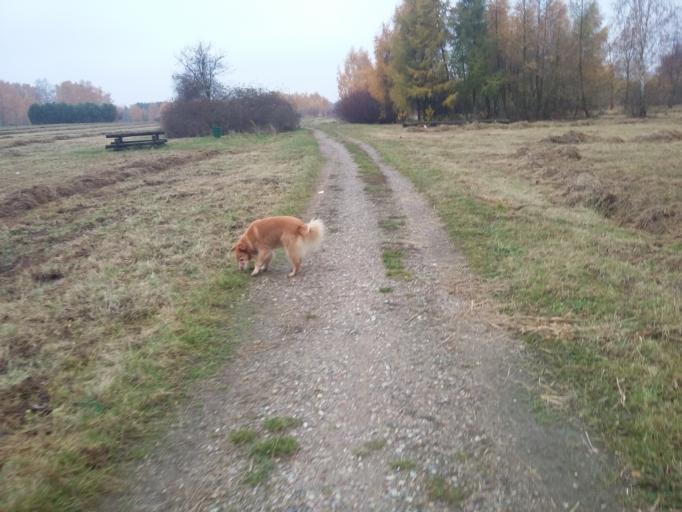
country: PL
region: Lodz Voivodeship
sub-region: Powiat pabianicki
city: Ksawerow
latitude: 51.7331
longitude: 19.3847
